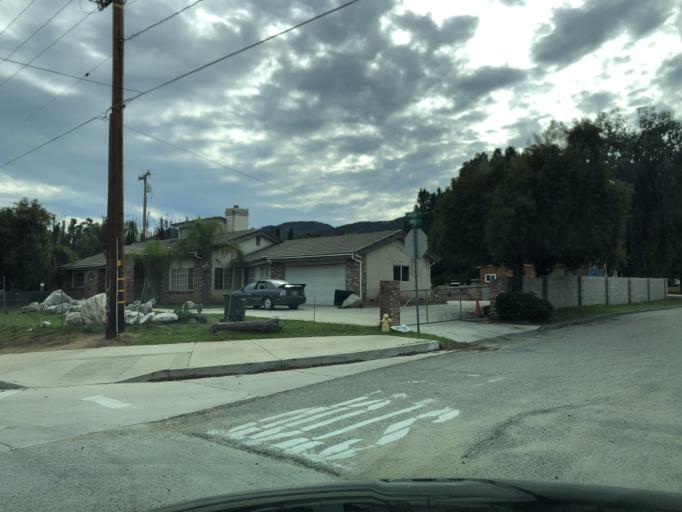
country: US
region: California
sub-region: Riverside County
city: Wildomar
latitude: 33.6056
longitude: -117.2908
